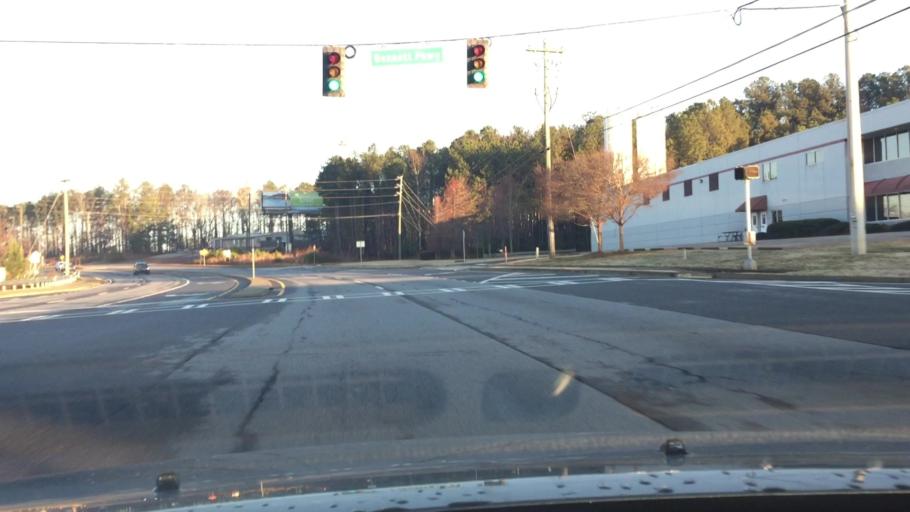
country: US
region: Georgia
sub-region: Forsyth County
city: Cumming
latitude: 34.1686
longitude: -84.1790
